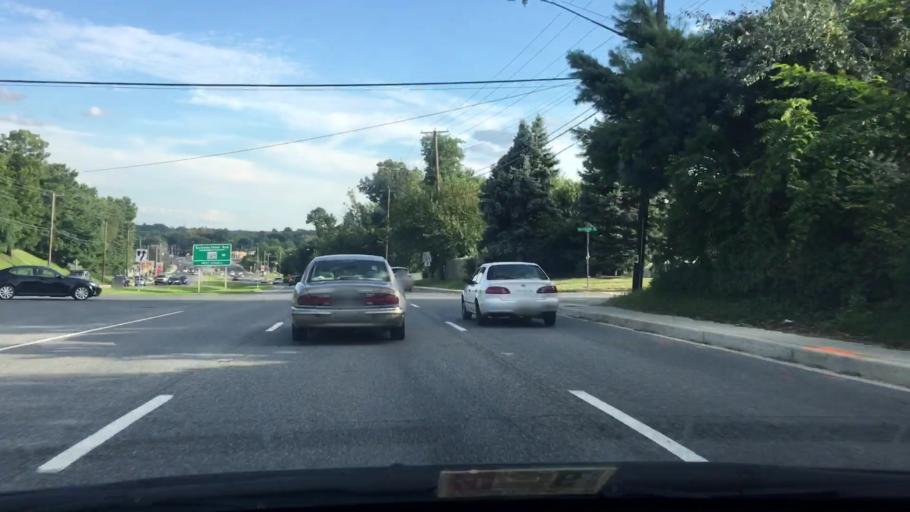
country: US
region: Maryland
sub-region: Montgomery County
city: Aspen Hill
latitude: 39.0879
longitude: -77.0799
